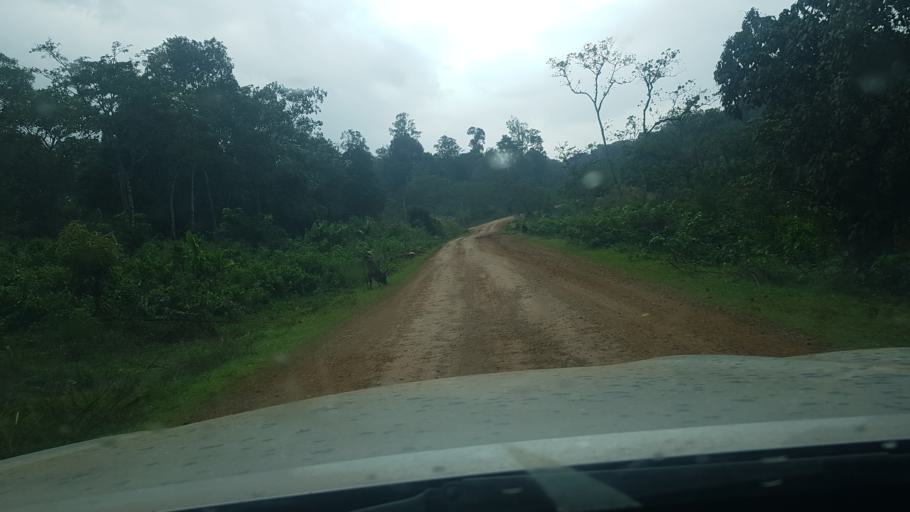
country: ET
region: Oromiya
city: Gore
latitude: 7.8763
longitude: 35.4824
